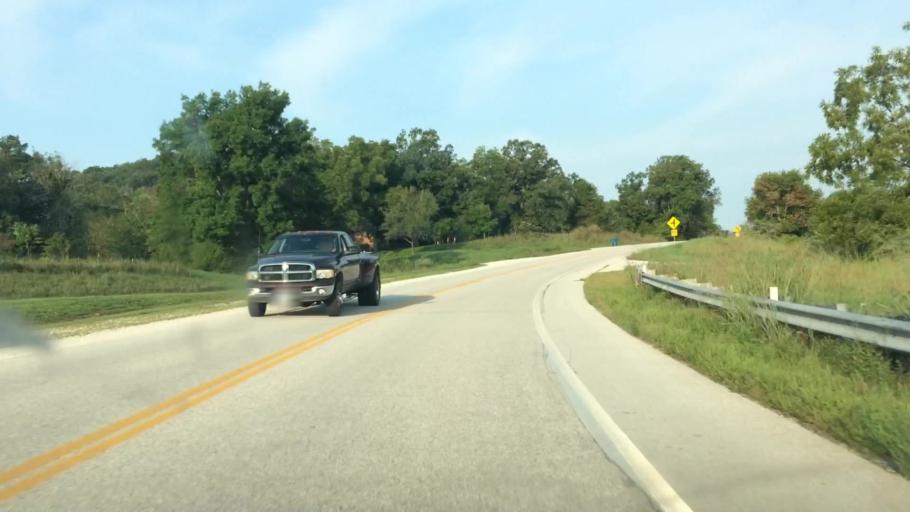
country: US
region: Missouri
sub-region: Greene County
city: Strafford
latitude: 37.1909
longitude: -93.1067
